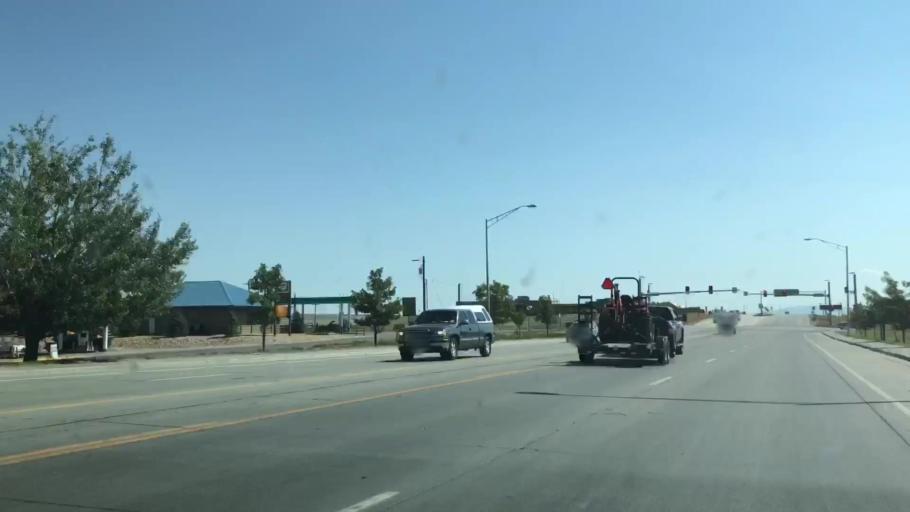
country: US
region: Wyoming
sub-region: Carbon County
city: Rawlins
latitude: 41.7924
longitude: -107.2108
